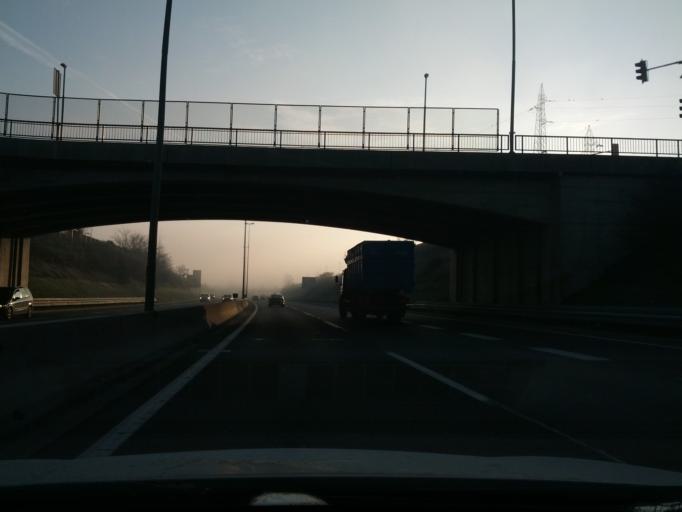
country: SI
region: Ljubljana
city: Ljubljana
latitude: 46.0783
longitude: 14.5343
